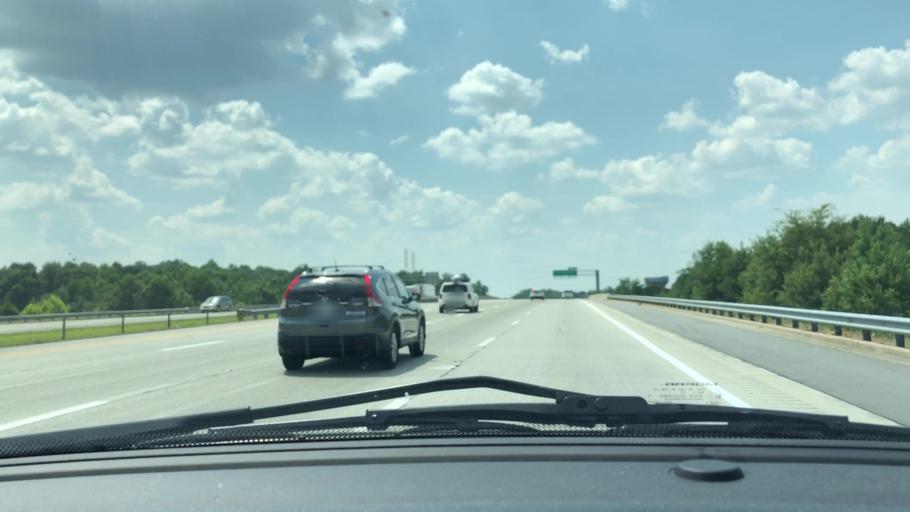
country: US
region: North Carolina
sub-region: Guilford County
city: Pleasant Garden
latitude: 35.9991
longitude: -79.7760
